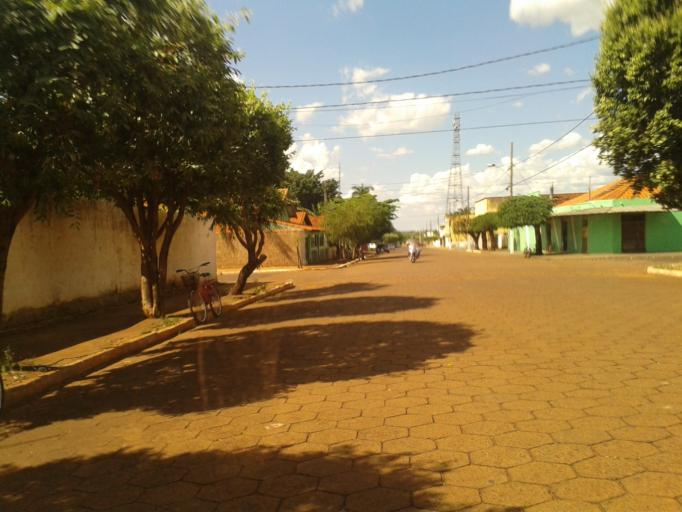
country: BR
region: Minas Gerais
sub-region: Santa Vitoria
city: Santa Vitoria
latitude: -18.6938
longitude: -49.9463
